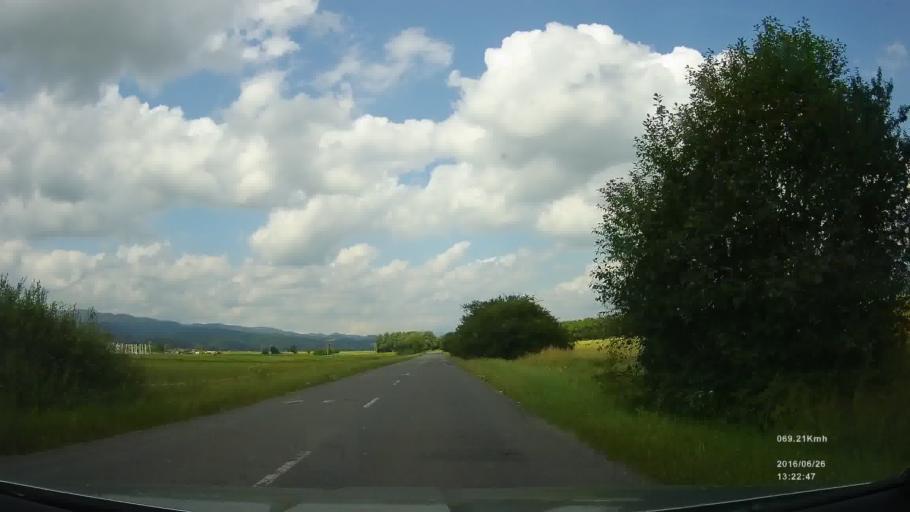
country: SK
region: Banskobystricky
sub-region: Okres Banska Bystrica
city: Zvolen
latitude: 48.6217
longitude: 19.1274
